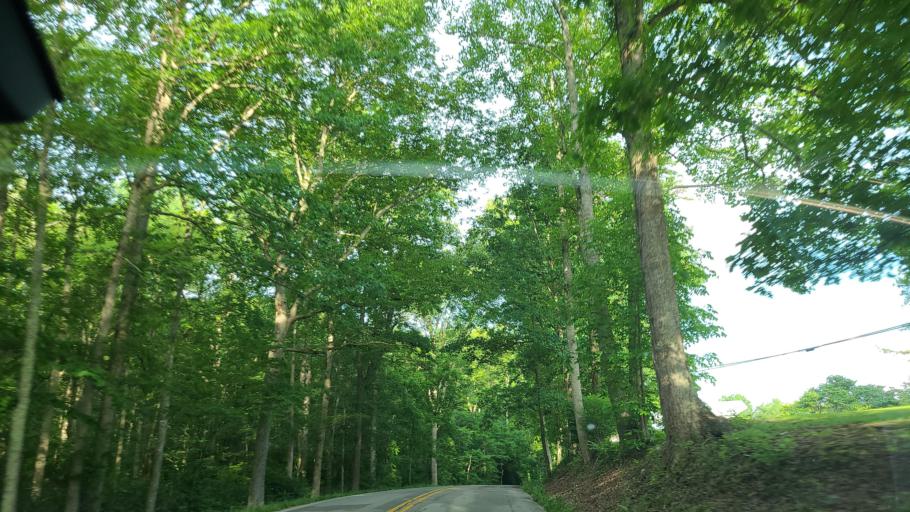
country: US
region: Kentucky
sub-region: Whitley County
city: Corbin
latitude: 36.8916
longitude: -84.2216
